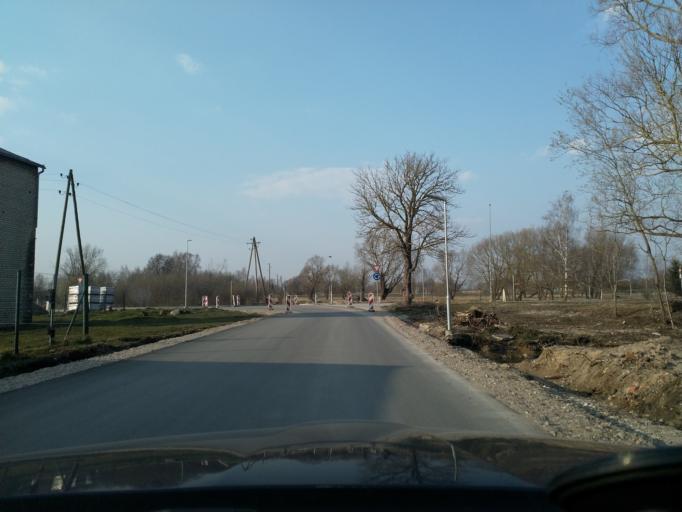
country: LV
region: Grobina
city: Grobina
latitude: 56.5351
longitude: 21.1823
